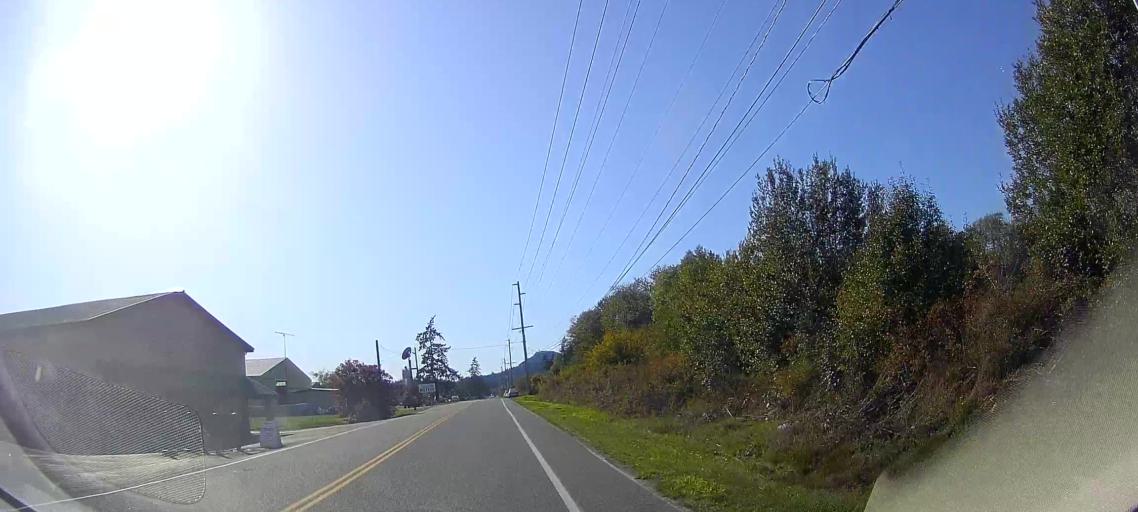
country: US
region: Washington
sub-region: Skagit County
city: Anacortes
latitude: 48.4639
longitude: -122.5467
